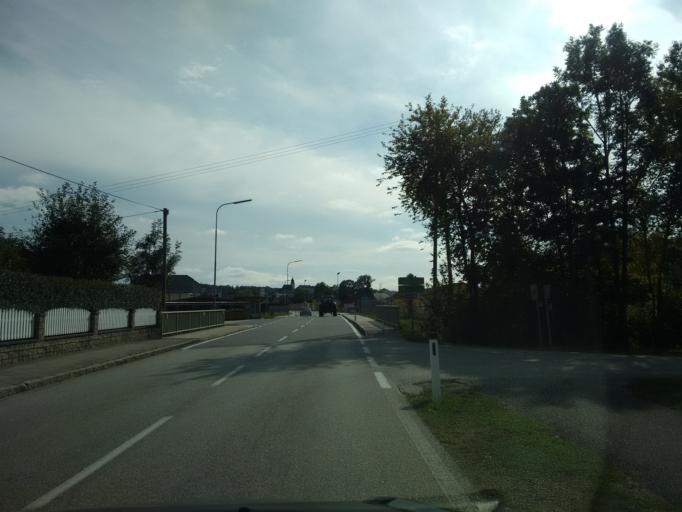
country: AT
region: Upper Austria
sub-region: Politischer Bezirk Steyr-Land
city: Bad Hall
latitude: 48.0726
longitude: 14.1902
